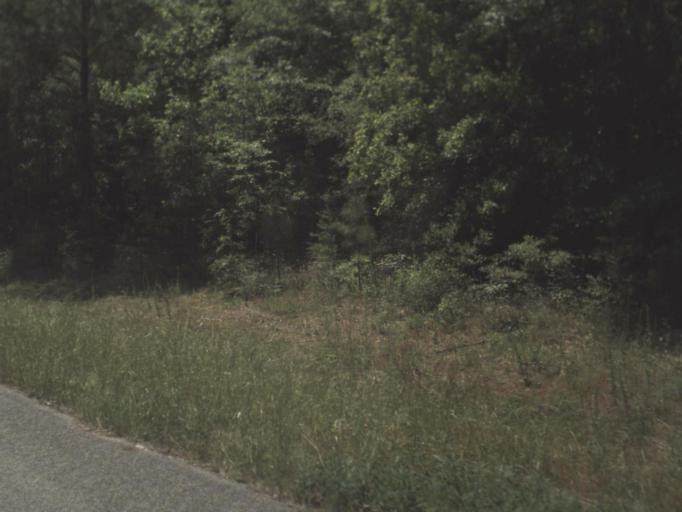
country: US
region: Florida
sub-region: Jackson County
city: Marianna
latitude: 30.6401
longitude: -85.1964
